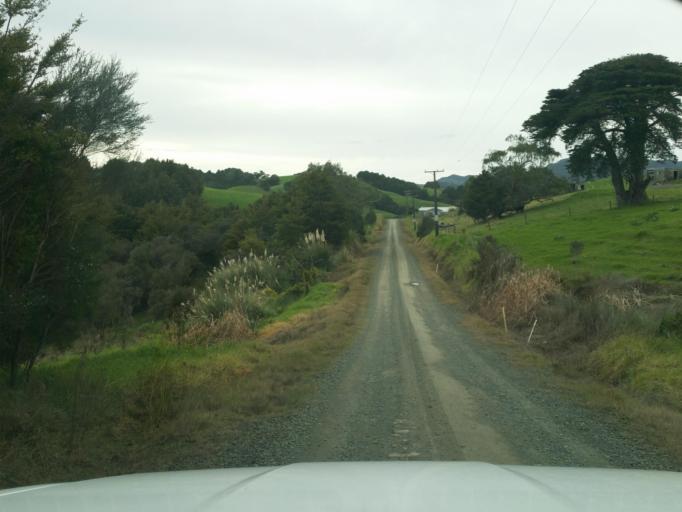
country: NZ
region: Northland
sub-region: Kaipara District
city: Dargaville
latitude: -35.8808
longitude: 173.9975
